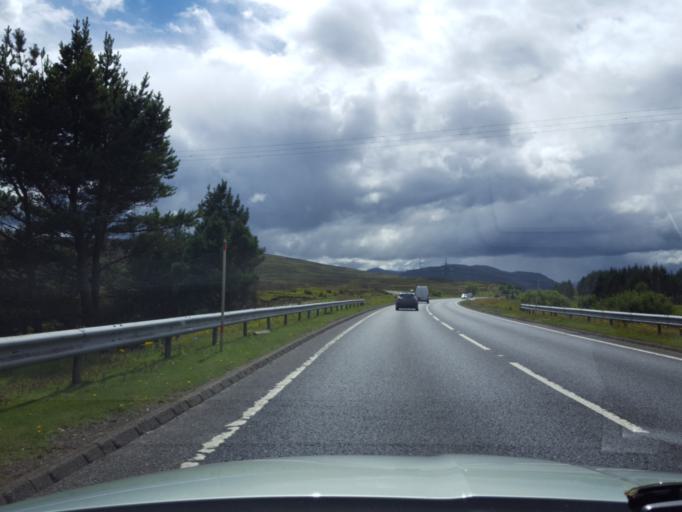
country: GB
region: Scotland
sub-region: Highland
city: Kingussie
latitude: 56.9543
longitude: -4.2111
